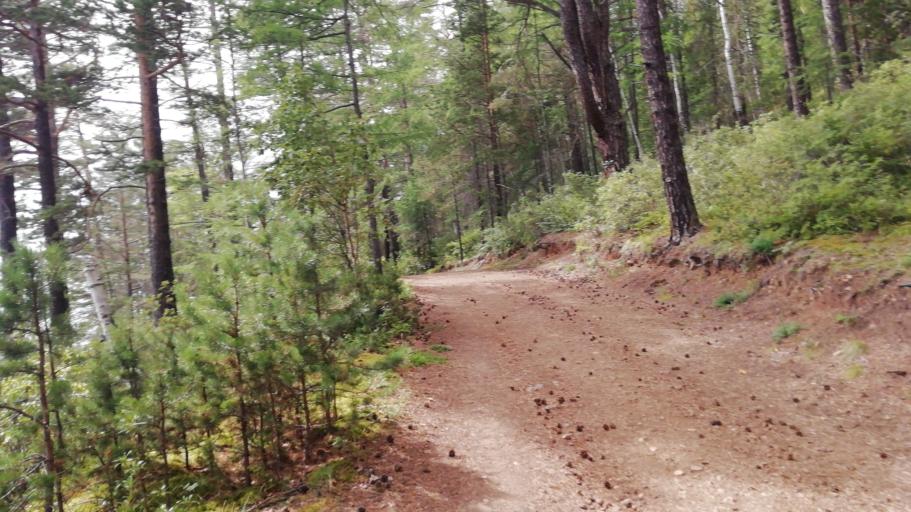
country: RU
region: Irkutsk
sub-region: Irkutskiy Rayon
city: Listvyanka
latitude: 51.8920
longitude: 105.0451
